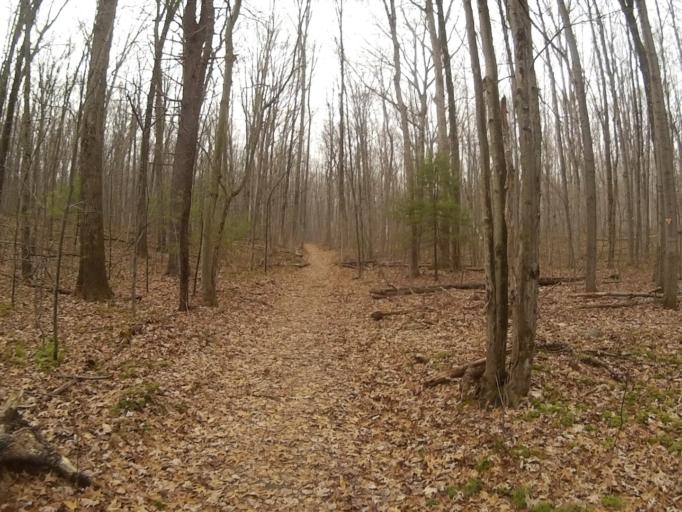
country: US
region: Pennsylvania
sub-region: Centre County
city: Park Forest Village
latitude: 40.7862
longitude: -77.9196
